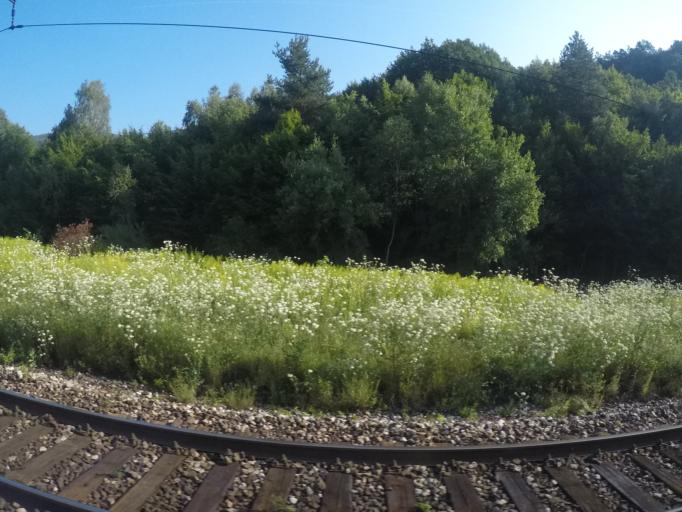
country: SK
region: Kosicky
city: Gelnica
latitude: 48.8929
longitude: 21.0203
